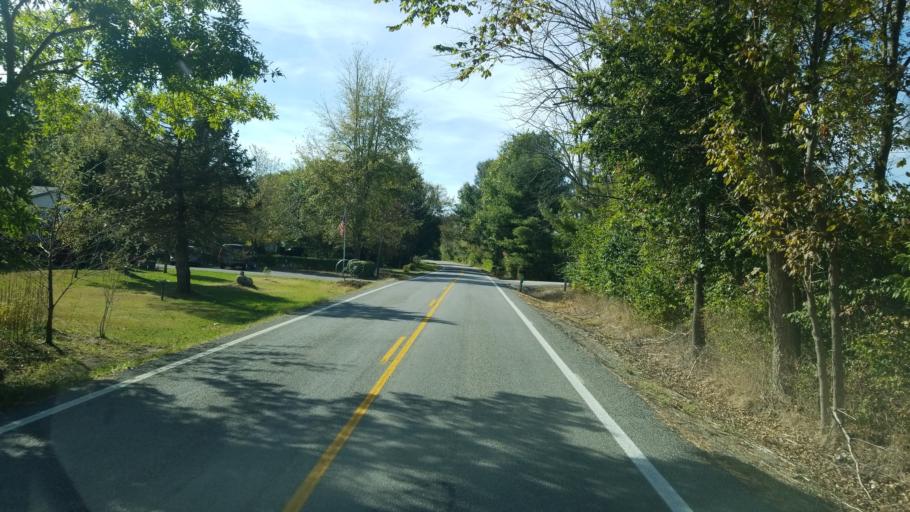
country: US
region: Ohio
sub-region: Clinton County
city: Blanchester
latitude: 39.4070
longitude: -84.0167
